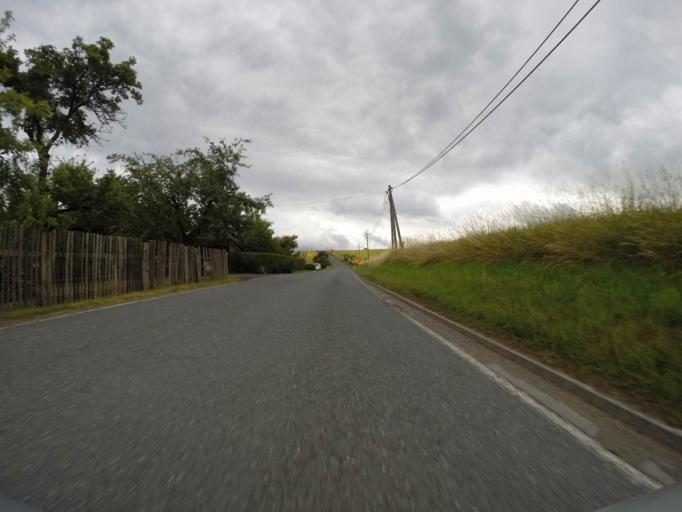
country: DE
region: Thuringia
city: Nausnitz
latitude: 50.9400
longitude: 11.7287
